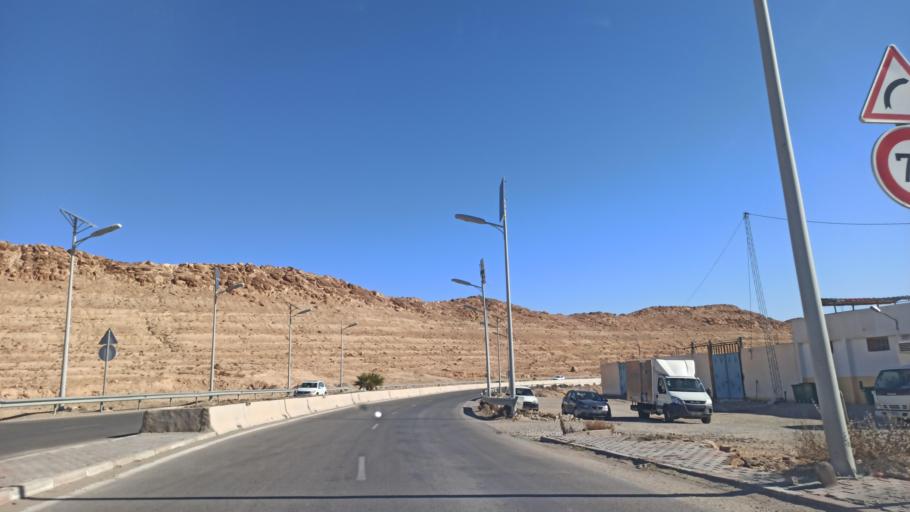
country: TN
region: Gafsa
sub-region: Gafsa Municipality
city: Gafsa
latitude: 34.4519
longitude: 8.7770
